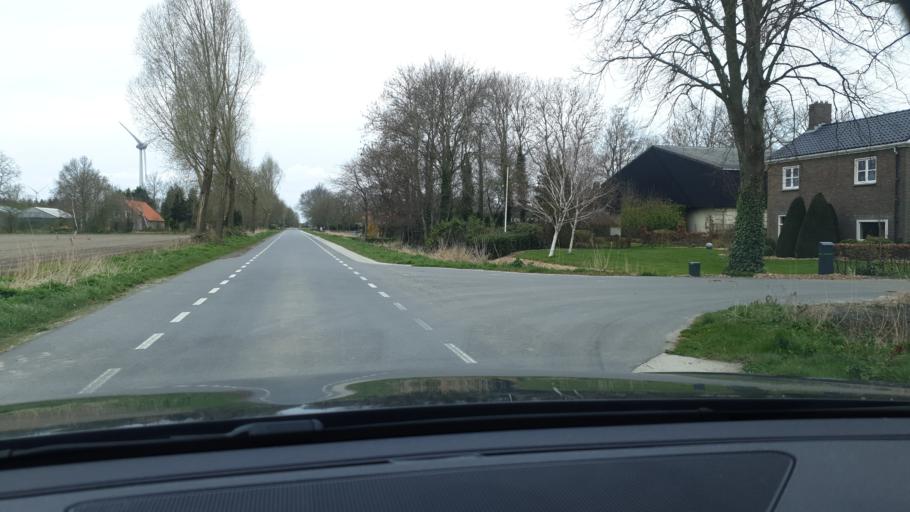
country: NL
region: Friesland
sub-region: Gemeente Lemsterland
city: Lemmer
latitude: 52.7770
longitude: 5.6331
